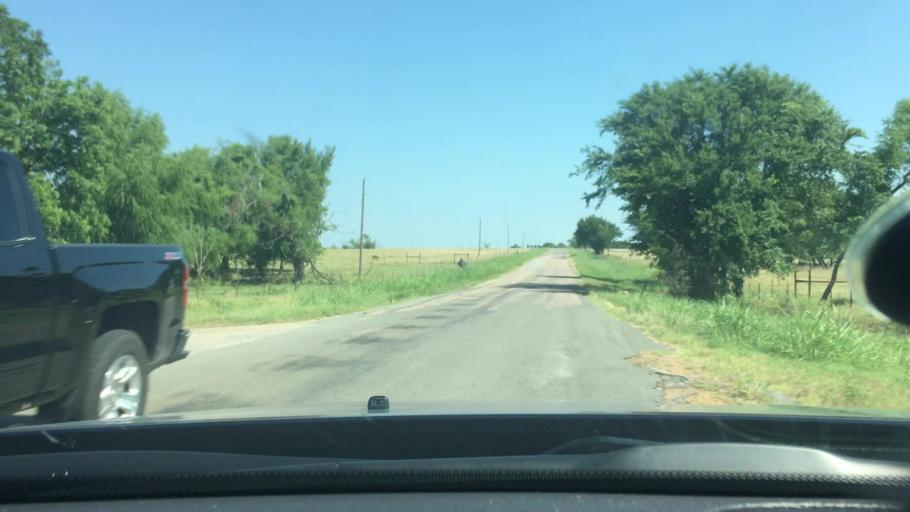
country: US
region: Oklahoma
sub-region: Johnston County
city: Tishomingo
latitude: 34.3118
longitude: -96.6360
